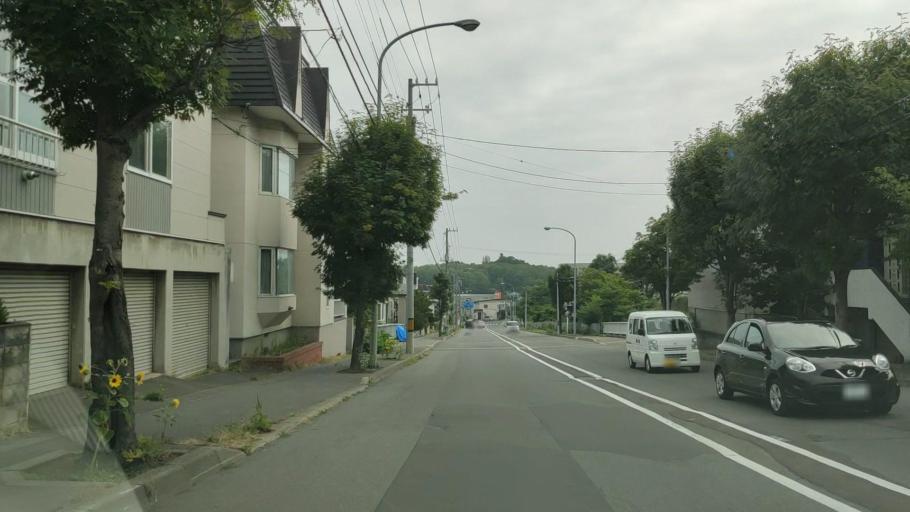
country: JP
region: Hokkaido
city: Otaru
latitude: 43.1838
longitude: 140.9846
